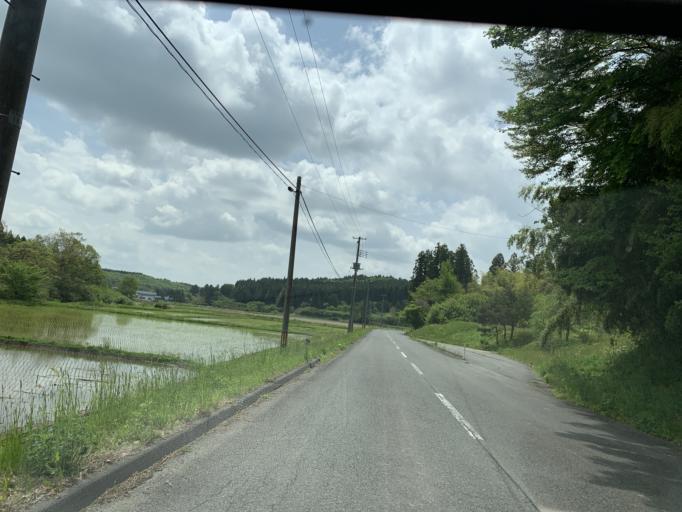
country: JP
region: Miyagi
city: Furukawa
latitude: 38.7056
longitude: 140.9185
